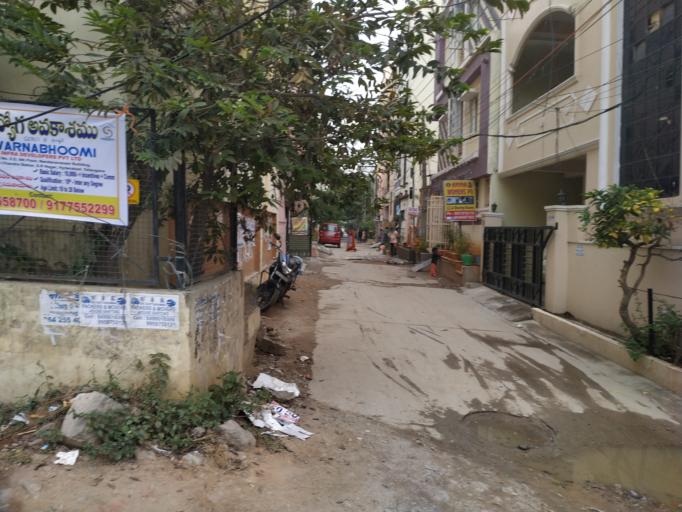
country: IN
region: Telangana
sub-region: Rangareddi
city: Kukatpalli
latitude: 17.4946
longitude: 78.3968
